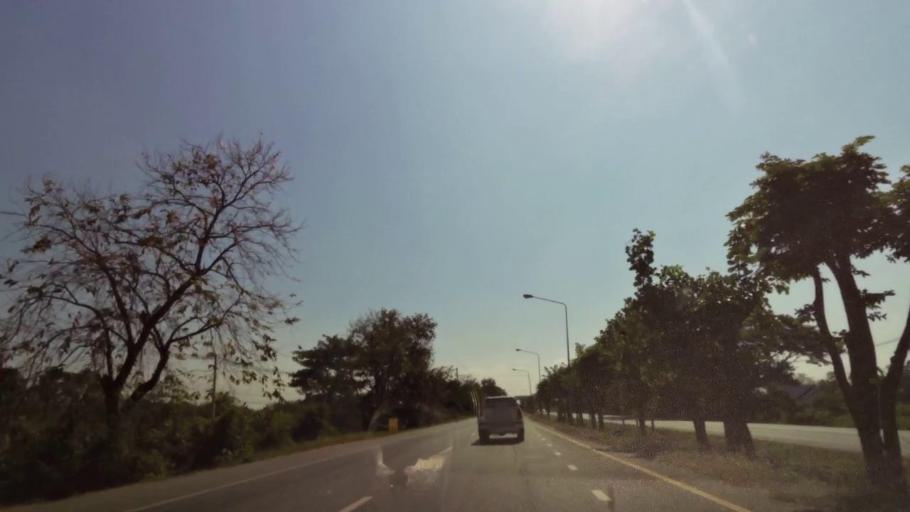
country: TH
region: Nakhon Sawan
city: Kao Liao
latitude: 15.7966
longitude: 100.1206
